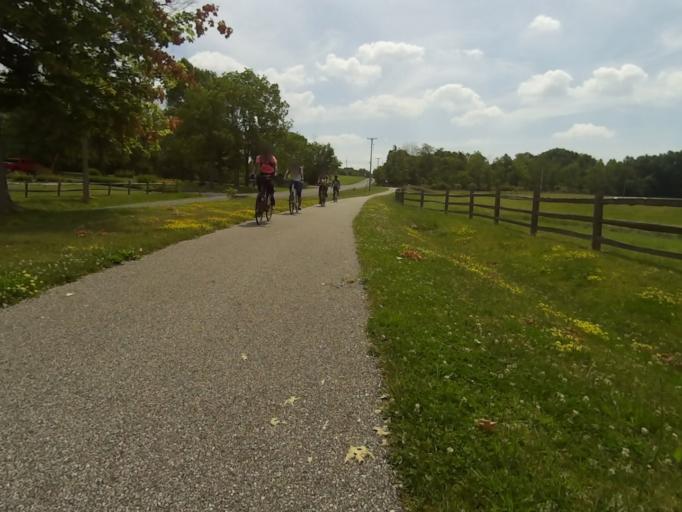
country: US
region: Ohio
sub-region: Summit County
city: Boston Heights
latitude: 41.2739
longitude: -81.5319
